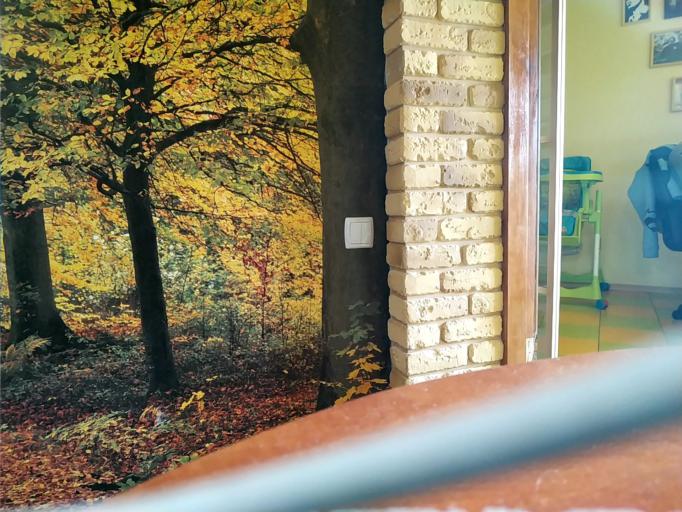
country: RU
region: Tverskaya
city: Rameshki
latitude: 57.2860
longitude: 35.9166
